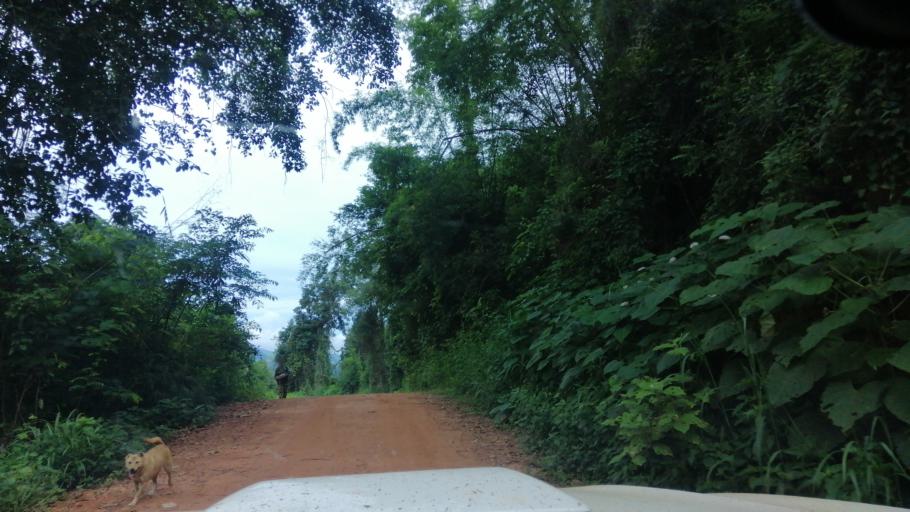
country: TH
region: Loei
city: Na Haeo
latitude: 17.5991
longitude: 101.1234
